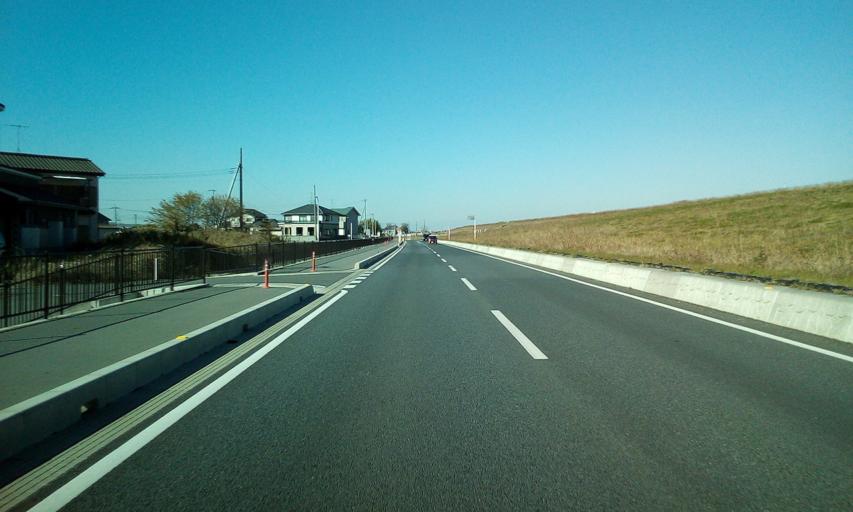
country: JP
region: Chiba
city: Noda
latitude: 35.9303
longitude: 139.8563
